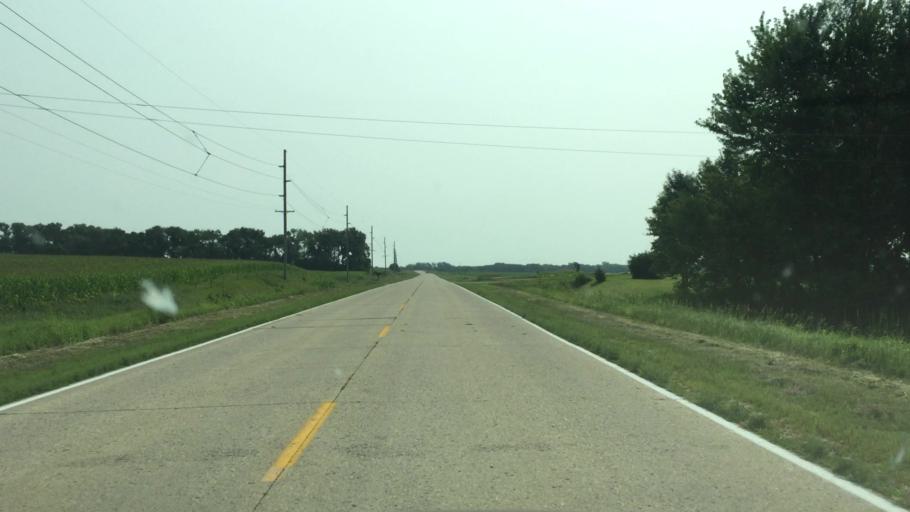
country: US
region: Iowa
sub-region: Dickinson County
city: Milford
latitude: 43.3714
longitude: -95.1960
